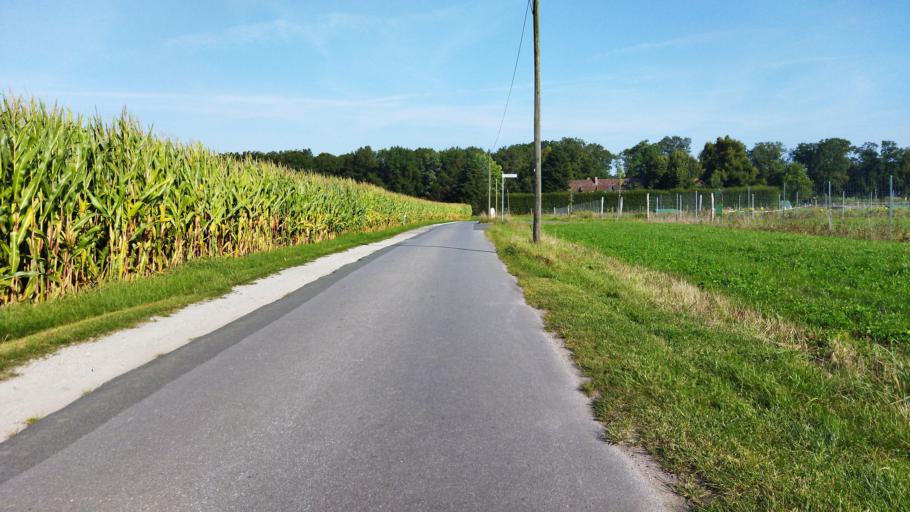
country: DE
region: Lower Saxony
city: Bad Laer
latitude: 52.1163
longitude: 8.0747
